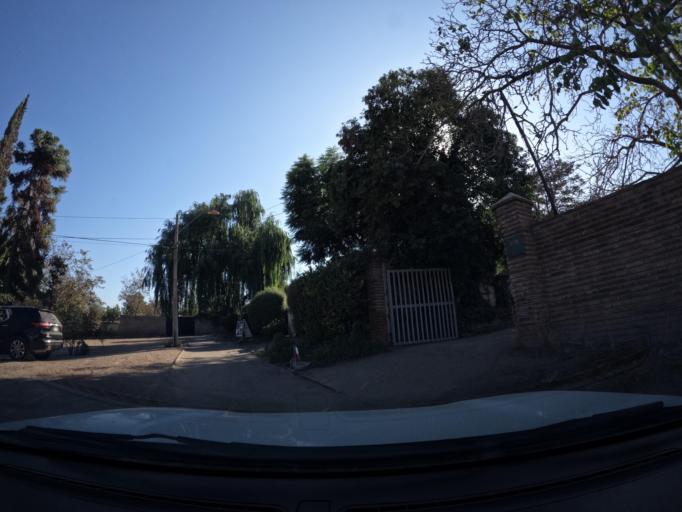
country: CL
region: Santiago Metropolitan
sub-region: Provincia de Santiago
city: Villa Presidente Frei, Nunoa, Santiago, Chile
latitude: -33.4954
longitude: -70.5473
